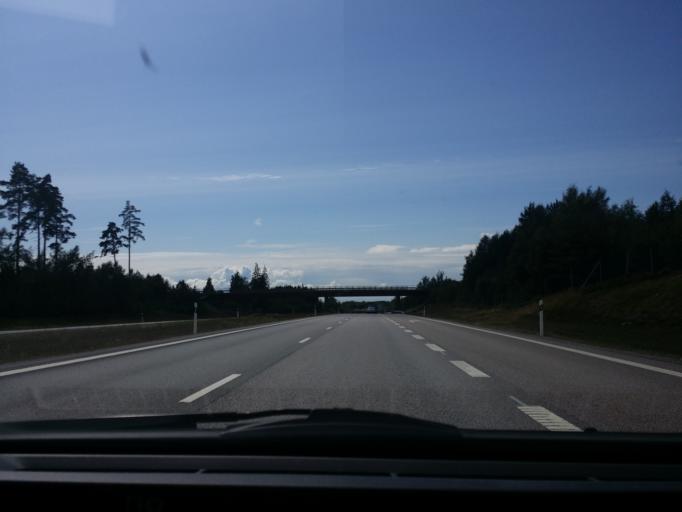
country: SE
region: OErebro
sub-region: Lindesbergs Kommun
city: Fellingsbro
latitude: 59.3417
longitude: 15.5436
